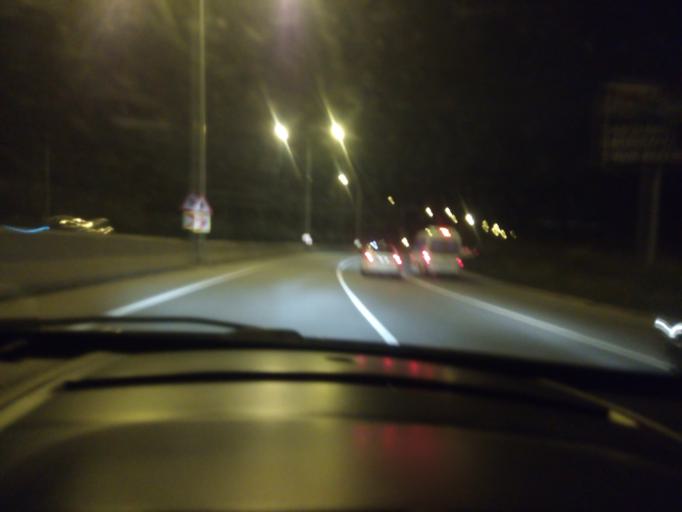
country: TR
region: Bursa
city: Niluefer
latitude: 40.3267
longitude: 28.9279
